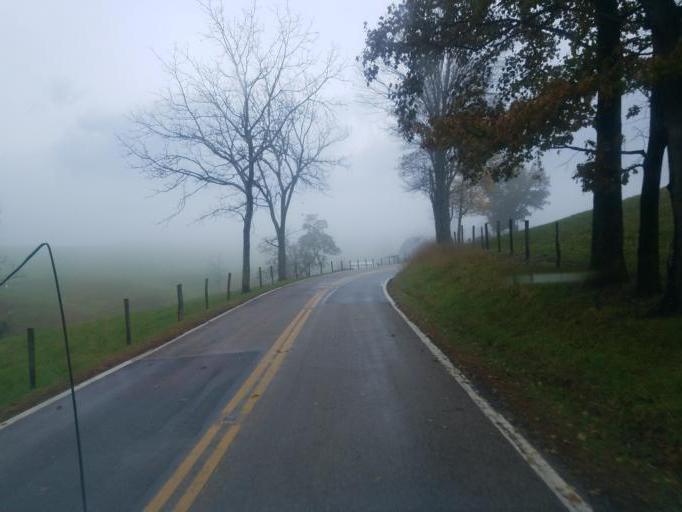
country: US
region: Ohio
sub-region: Morgan County
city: McConnelsville
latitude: 39.5143
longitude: -81.9174
